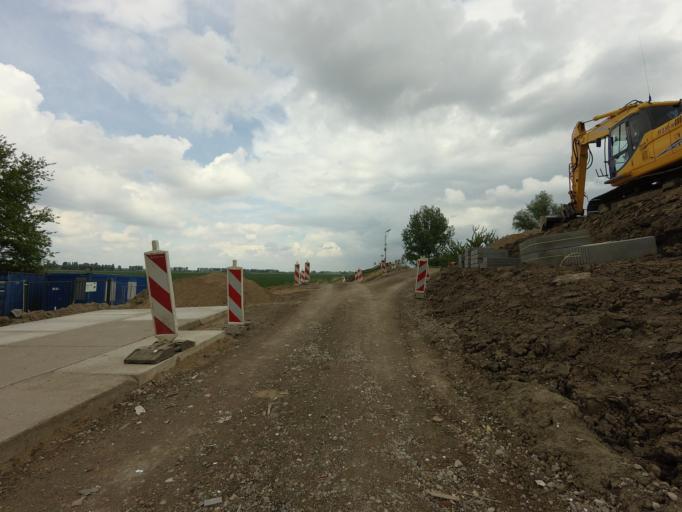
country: NL
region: South Holland
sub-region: Gemeente Strijen
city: Strijen
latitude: 51.7170
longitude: 4.5898
